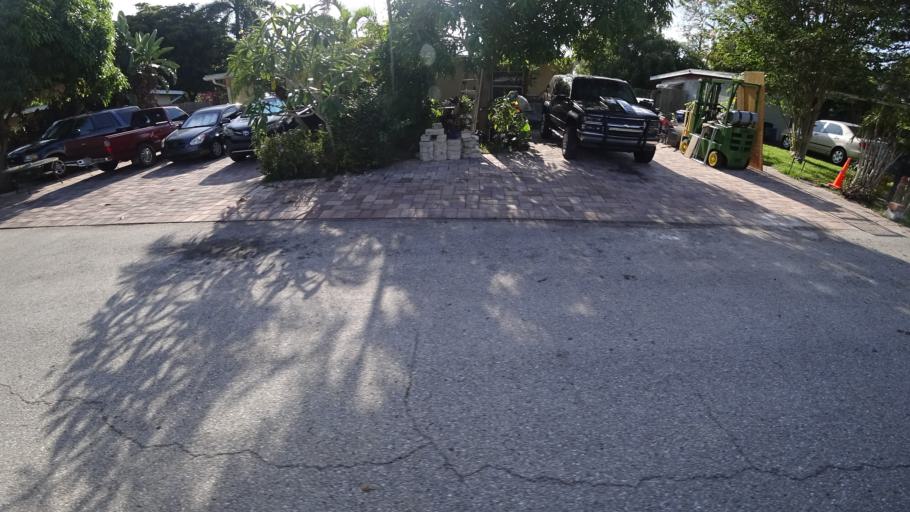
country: US
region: Florida
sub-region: Manatee County
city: West Samoset
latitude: 27.4449
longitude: -82.5595
